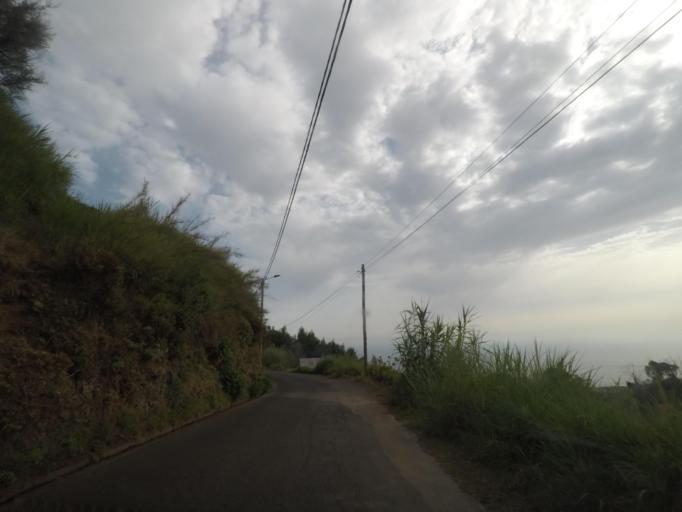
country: PT
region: Madeira
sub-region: Calheta
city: Arco da Calheta
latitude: 32.7358
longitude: -17.1537
